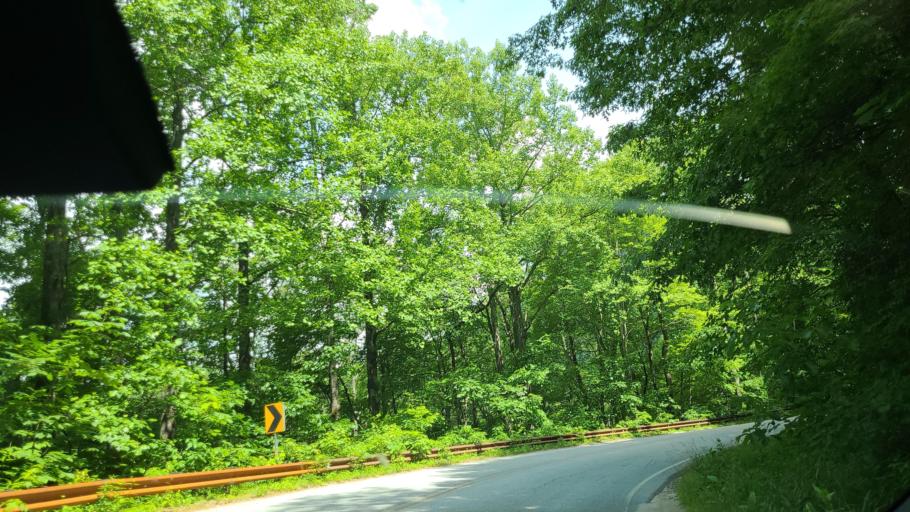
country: US
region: Georgia
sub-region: Rabun County
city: Mountain City
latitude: 35.0228
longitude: -83.1866
